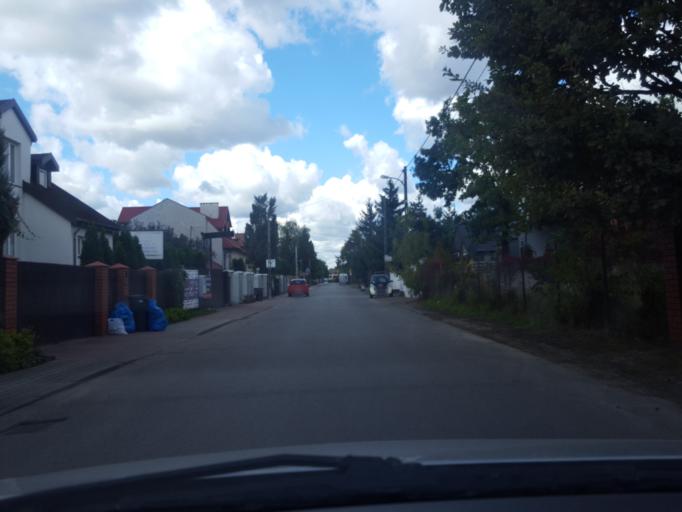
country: PL
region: Masovian Voivodeship
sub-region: Warszawa
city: Rembertow
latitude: 52.2714
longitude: 21.1668
